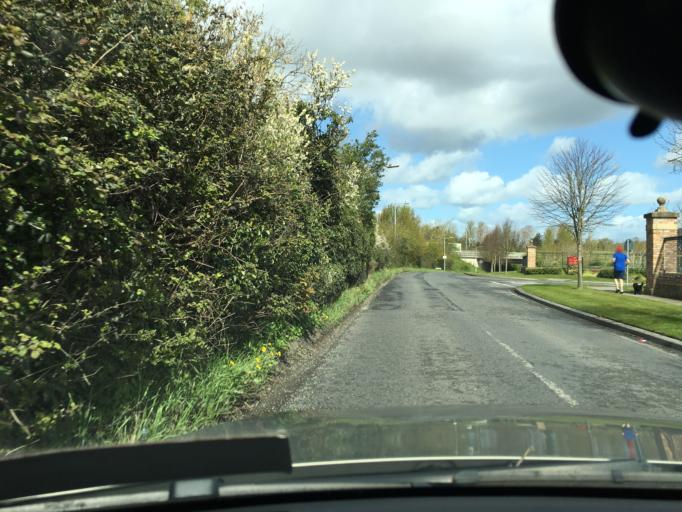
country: IE
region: Leinster
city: Castleknock
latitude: 53.3687
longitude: -6.3755
